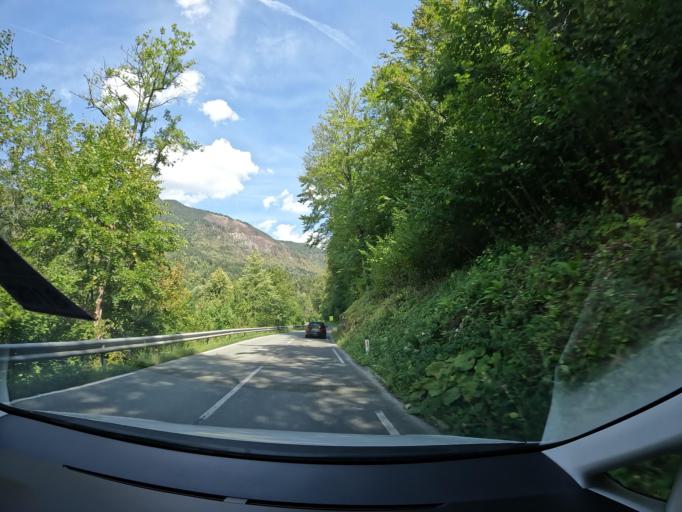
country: SI
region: Preddvor
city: Preddvor
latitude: 46.3012
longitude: 14.4347
